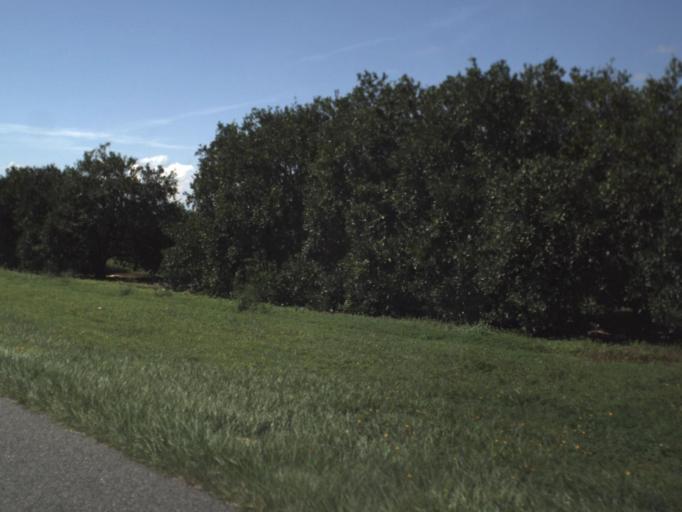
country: US
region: Florida
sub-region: Polk County
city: Dundee
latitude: 28.0051
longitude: -81.5950
